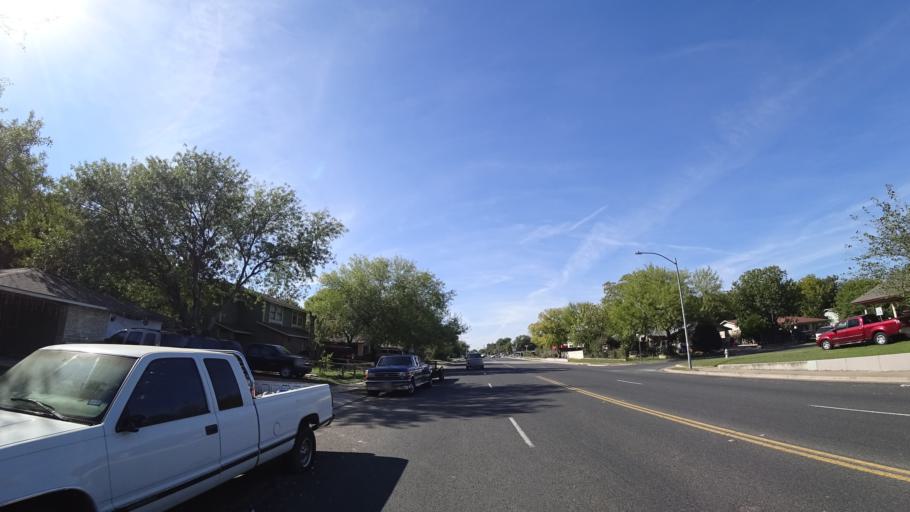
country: US
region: Texas
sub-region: Travis County
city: Austin
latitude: 30.1959
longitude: -97.7424
